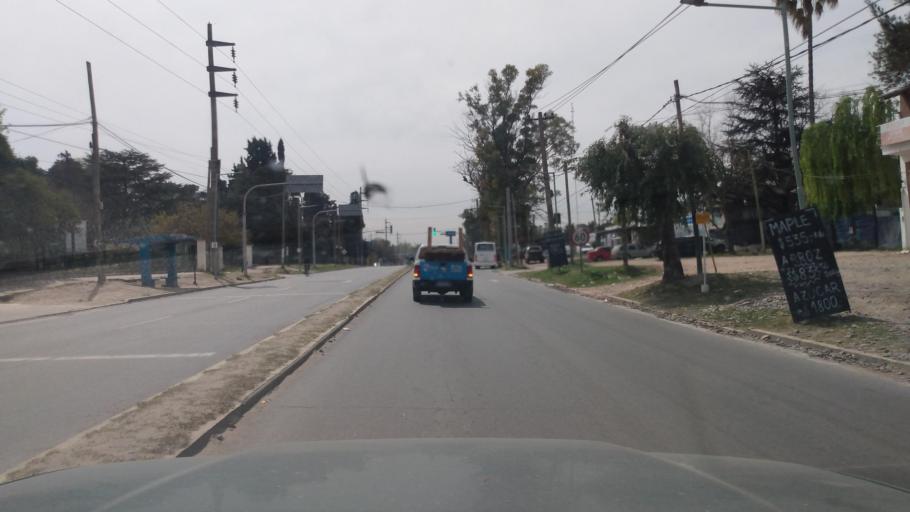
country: AR
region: Buenos Aires
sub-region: Partido de Pilar
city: Pilar
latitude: -34.4486
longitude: -58.9049
